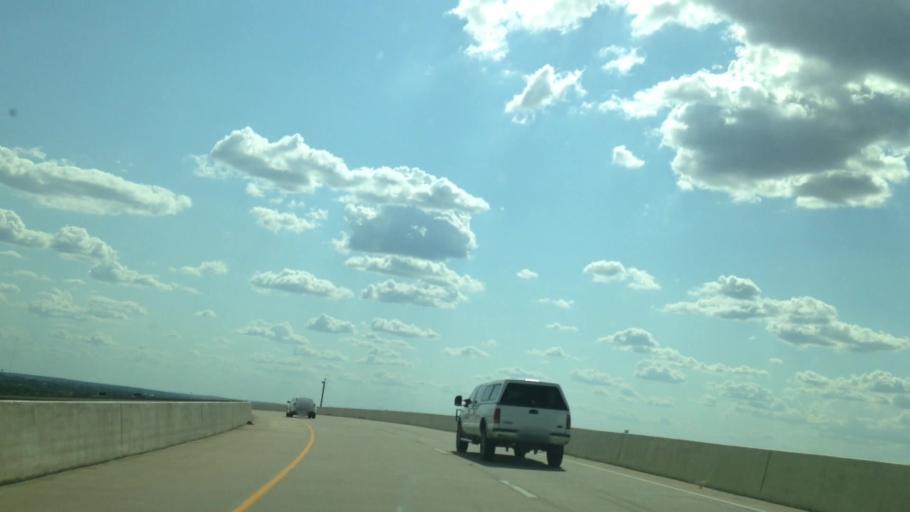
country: US
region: Texas
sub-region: Travis County
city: Onion Creek
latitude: 30.1117
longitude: -97.8064
